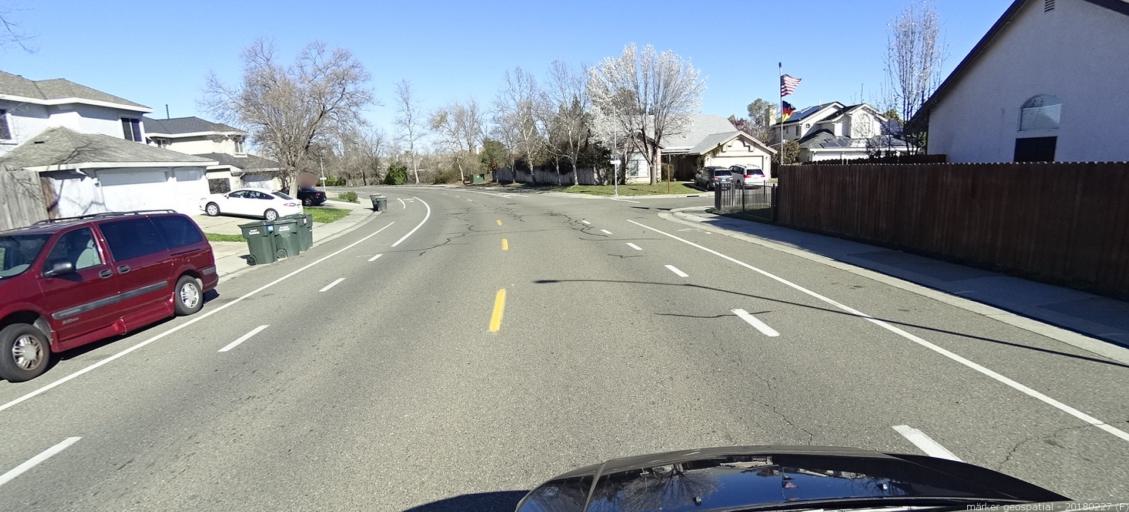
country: US
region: California
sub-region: Sacramento County
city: North Highlands
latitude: 38.7236
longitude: -121.3691
